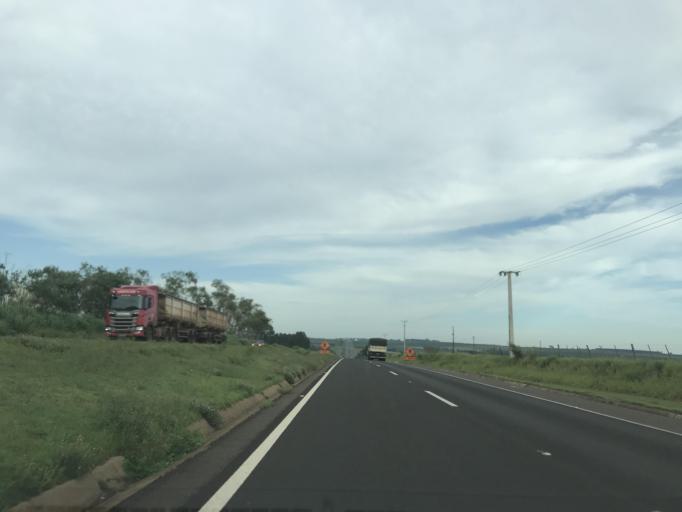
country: BR
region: Parana
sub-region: Alto Parana
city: Alto Parana
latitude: -23.1181
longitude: -52.3202
